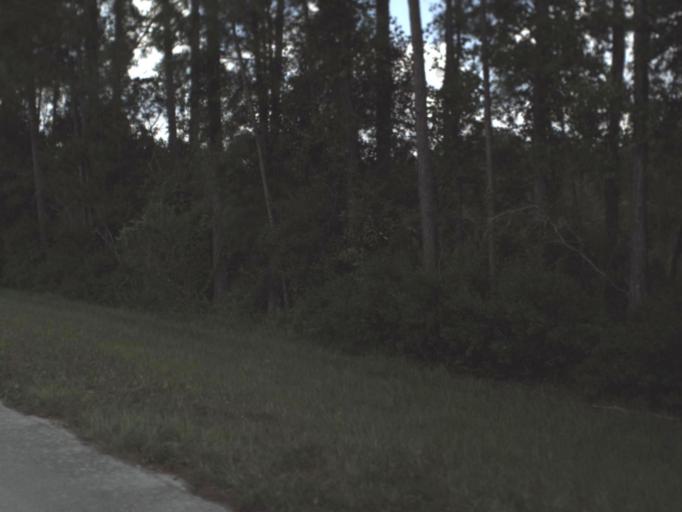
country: US
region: Florida
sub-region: Baker County
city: Macclenny
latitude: 30.1838
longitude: -82.1683
